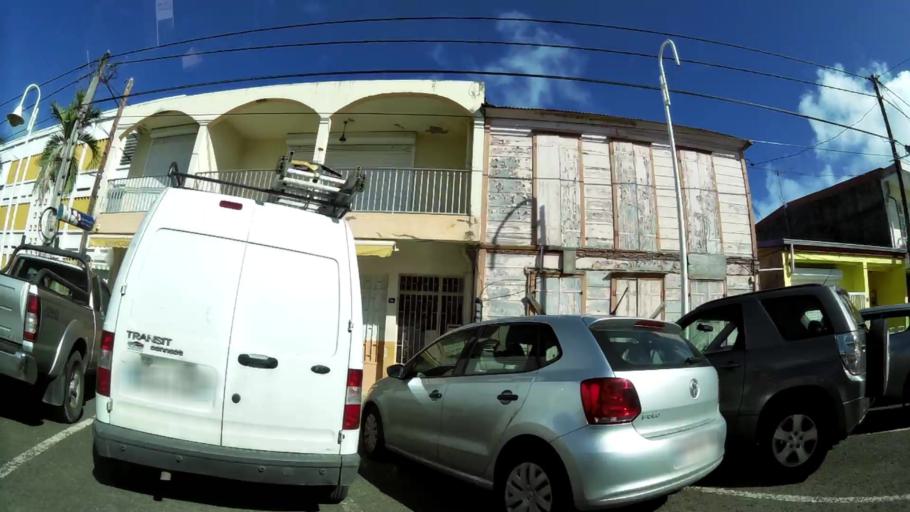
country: GP
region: Guadeloupe
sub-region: Guadeloupe
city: Sainte-Anne
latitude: 16.2250
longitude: -61.3853
